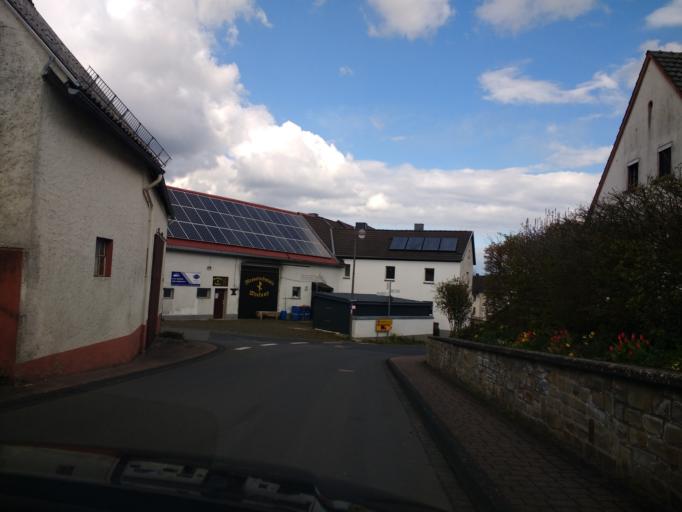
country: DE
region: Rheinland-Pfalz
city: Uxheim
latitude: 50.3425
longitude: 6.7440
